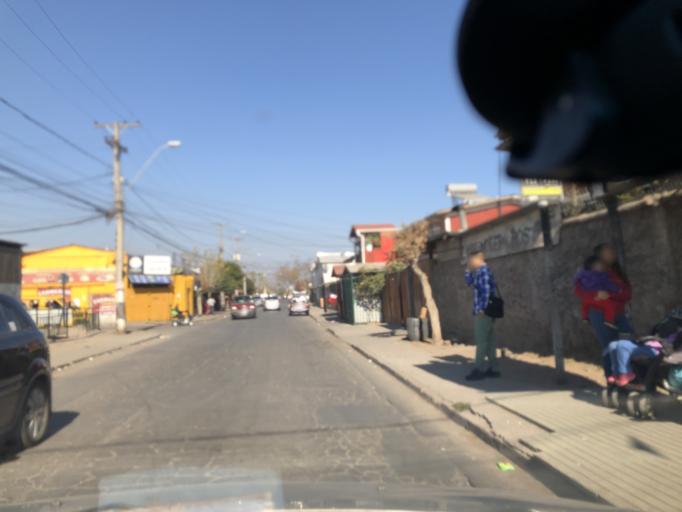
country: CL
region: Santiago Metropolitan
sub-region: Provincia de Cordillera
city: Puente Alto
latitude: -33.6221
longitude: -70.5965
